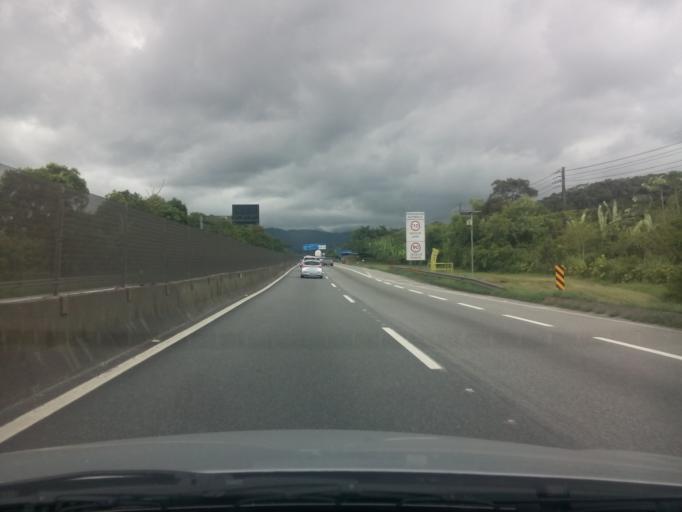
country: BR
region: Sao Paulo
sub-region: Santos
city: Santos
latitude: -23.9152
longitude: -46.2894
